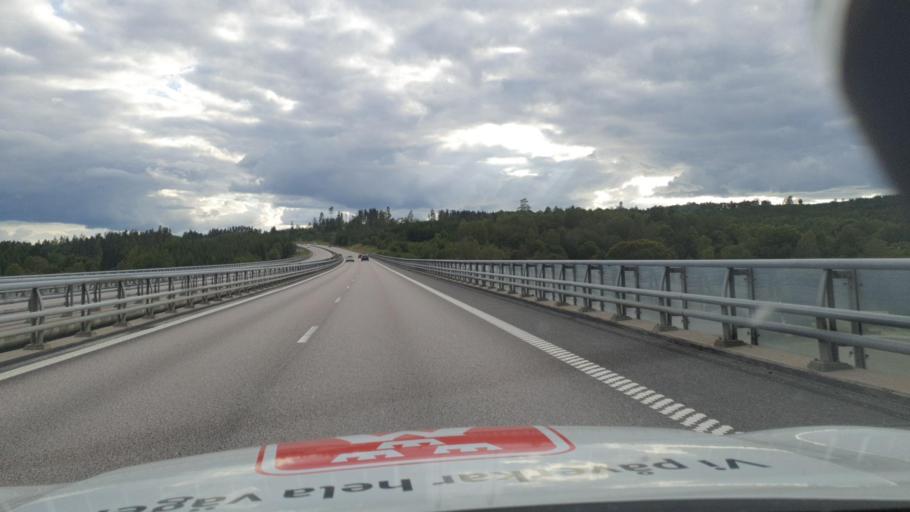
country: SE
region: Vaestra Goetaland
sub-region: Boras Kommun
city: Dalsjofors
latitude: 57.7880
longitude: 13.1277
